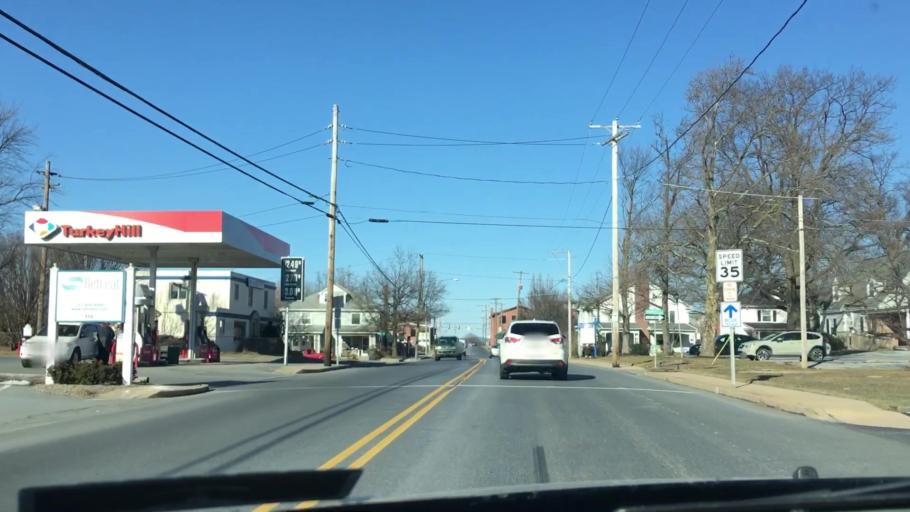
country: US
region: Pennsylvania
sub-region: Lancaster County
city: Akron
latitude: 40.1552
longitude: -76.2058
